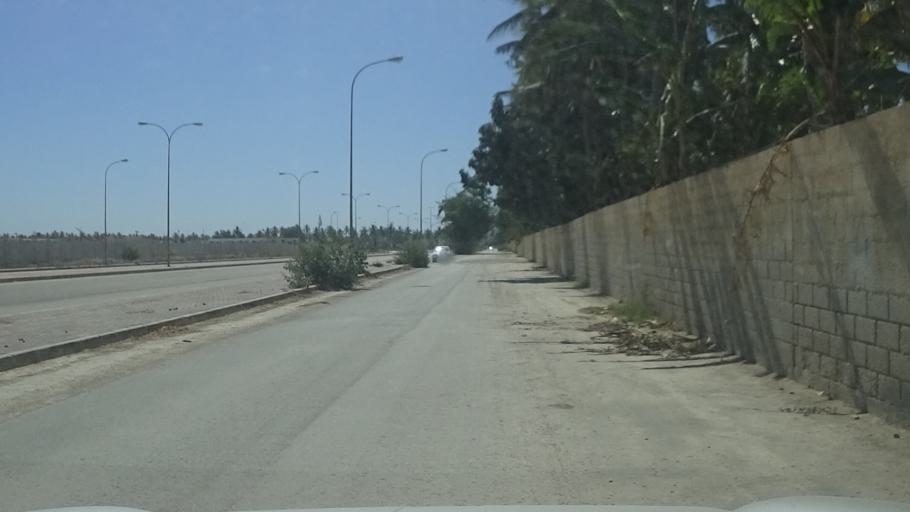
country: OM
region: Zufar
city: Salalah
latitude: 17.0296
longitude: 54.1226
